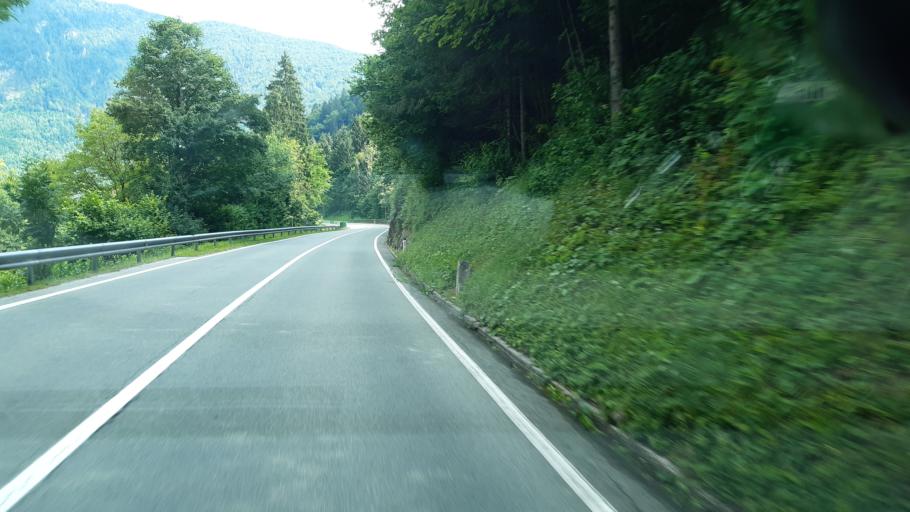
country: SI
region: Trzic
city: Trzic
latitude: 46.3726
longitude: 14.3020
